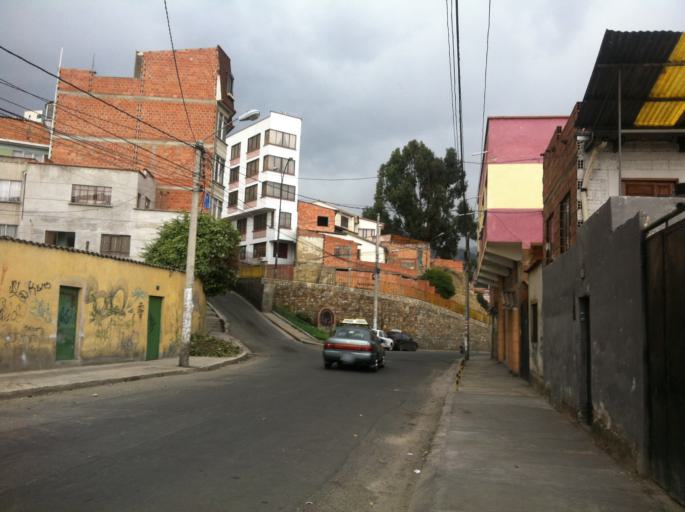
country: BO
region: La Paz
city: La Paz
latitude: -16.4938
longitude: -68.1197
